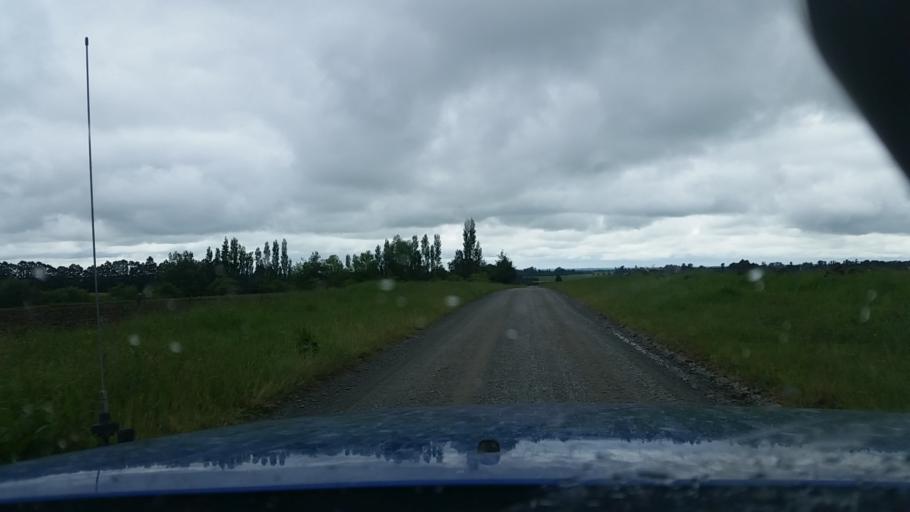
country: NZ
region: Canterbury
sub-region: Ashburton District
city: Methven
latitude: -43.6936
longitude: 171.4027
